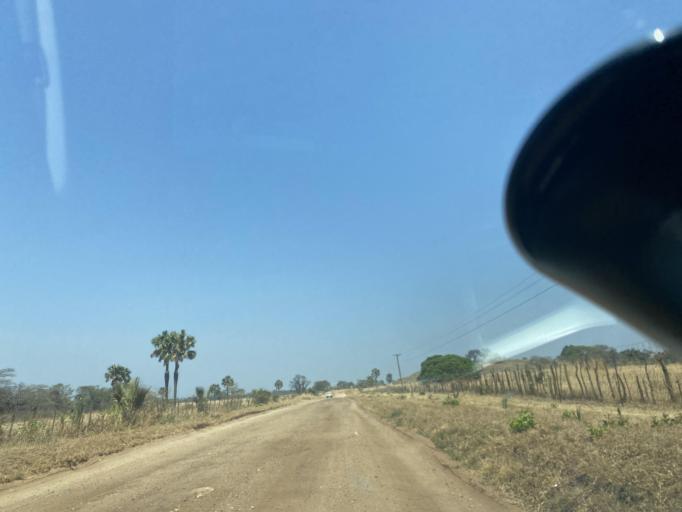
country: ZM
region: Lusaka
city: Lusaka
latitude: -15.5351
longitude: 28.0897
